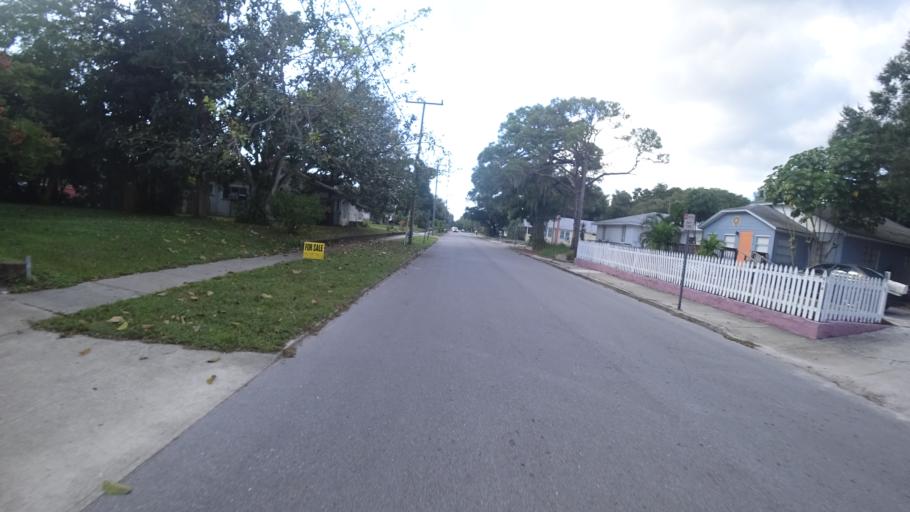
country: US
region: Florida
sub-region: Manatee County
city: Bradenton
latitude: 27.4891
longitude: -82.5779
